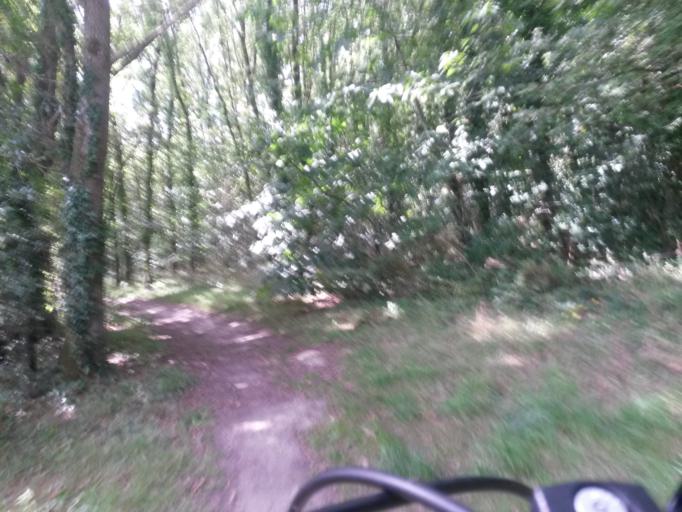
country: FR
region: Pays de la Loire
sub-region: Departement de la Loire-Atlantique
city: Asserac
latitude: 47.3857
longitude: -2.3627
